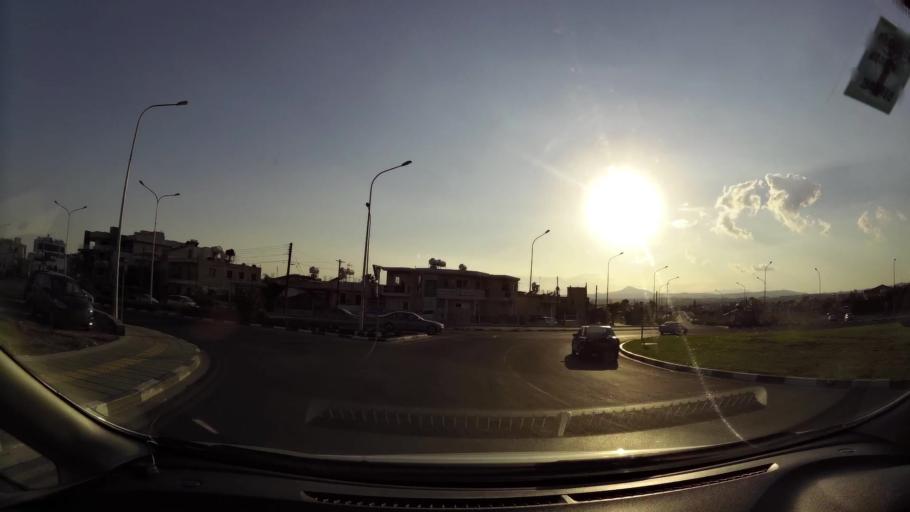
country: CY
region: Larnaka
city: Larnaca
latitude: 34.9216
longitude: 33.5997
